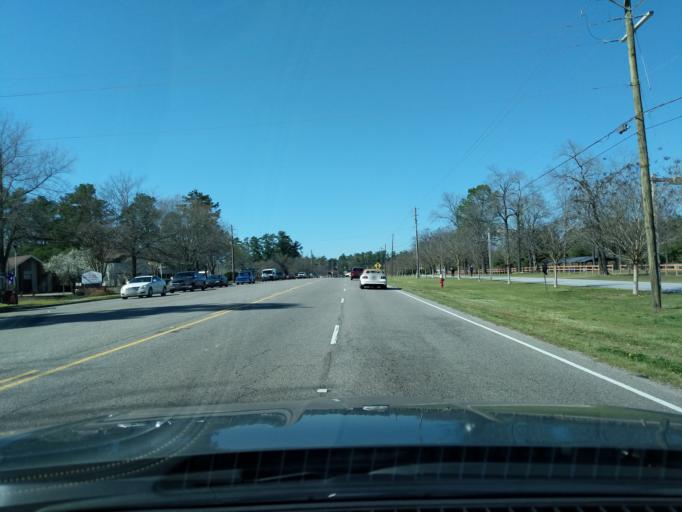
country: US
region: South Carolina
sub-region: Aiken County
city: Aiken
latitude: 33.5281
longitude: -81.7222
